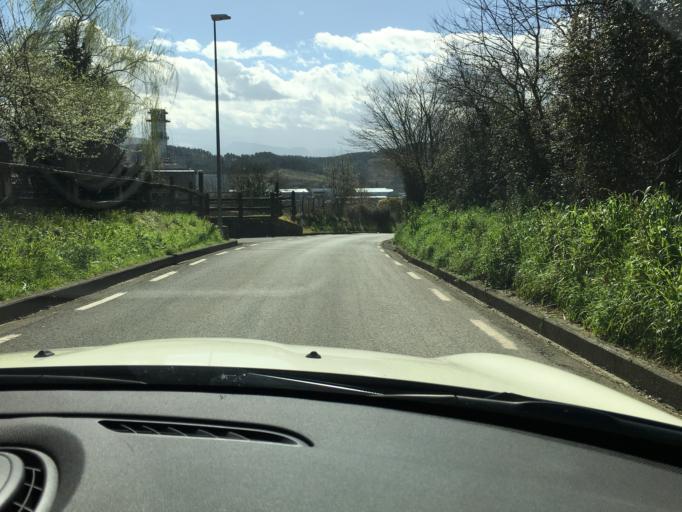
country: ES
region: Basque Country
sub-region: Bizkaia
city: Amorebieta
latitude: 43.2376
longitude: -2.7500
